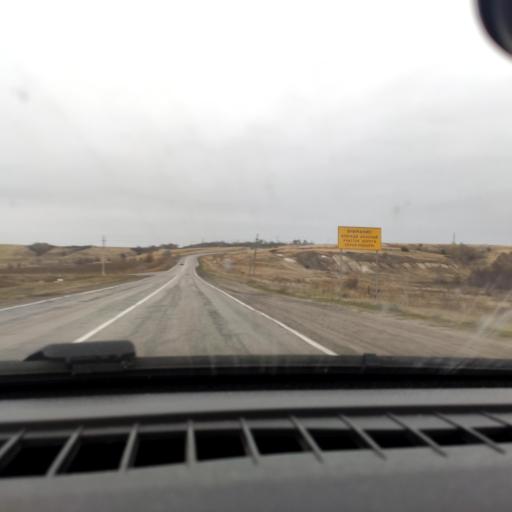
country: RU
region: Voronezj
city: Uryv-Pokrovka
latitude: 51.1316
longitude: 39.0448
